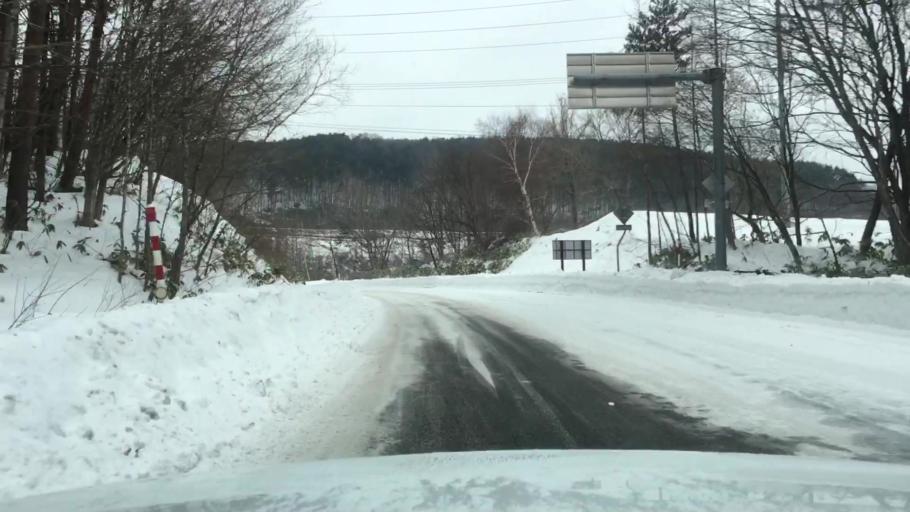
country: JP
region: Iwate
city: Shizukuishi
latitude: 39.9482
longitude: 140.9985
